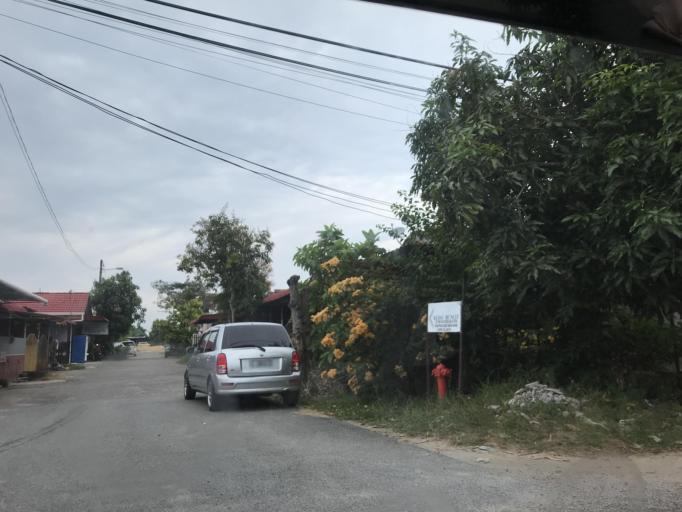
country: MY
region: Kelantan
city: Kota Bharu
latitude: 6.1149
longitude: 102.2109
